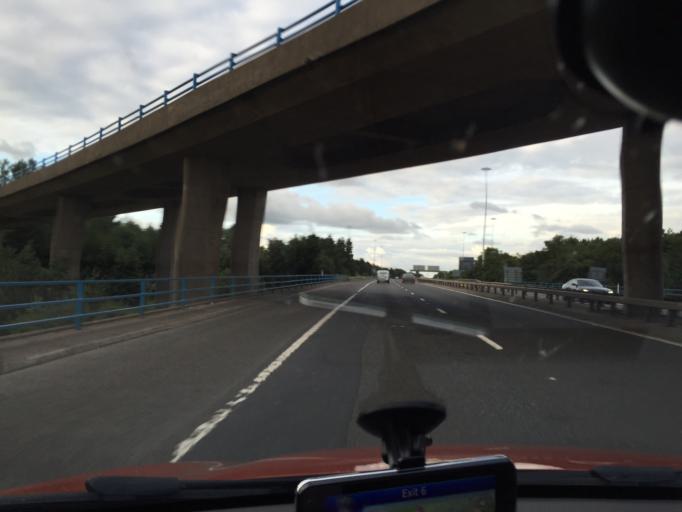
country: GB
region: Scotland
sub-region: South Lanarkshire
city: Uddingston
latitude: 55.8531
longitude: -4.0899
